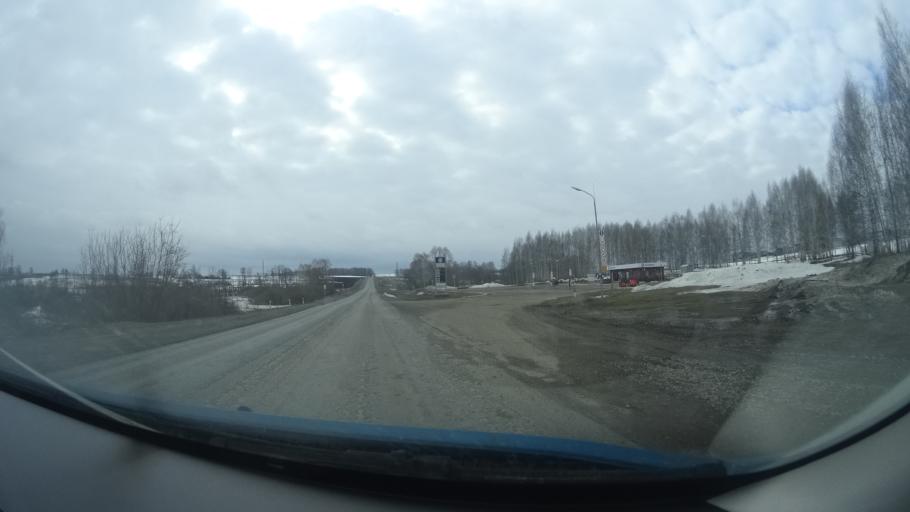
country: RU
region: Bashkortostan
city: Birsk
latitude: 55.4135
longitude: 55.5854
